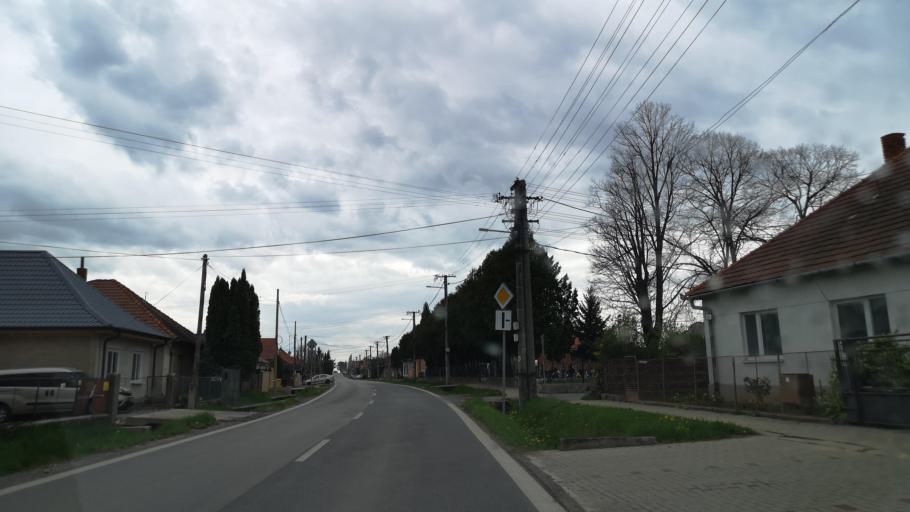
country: SK
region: Nitriansky
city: Zlate Moravce
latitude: 48.3331
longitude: 18.3532
